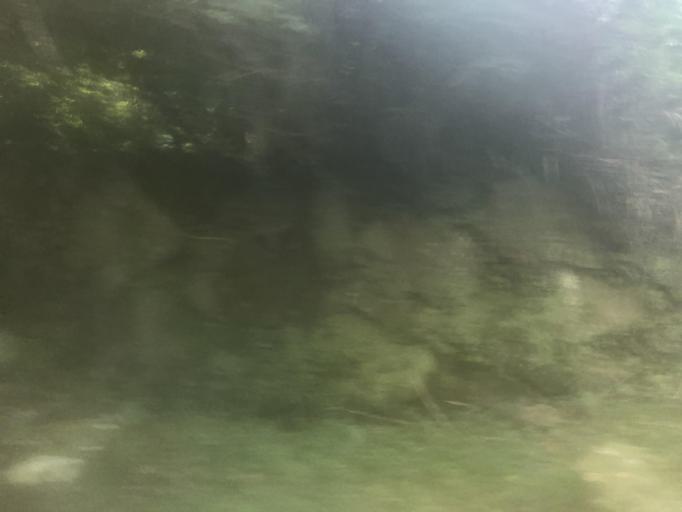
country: TW
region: Taiwan
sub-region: Keelung
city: Keelung
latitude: 25.1658
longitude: 121.6613
